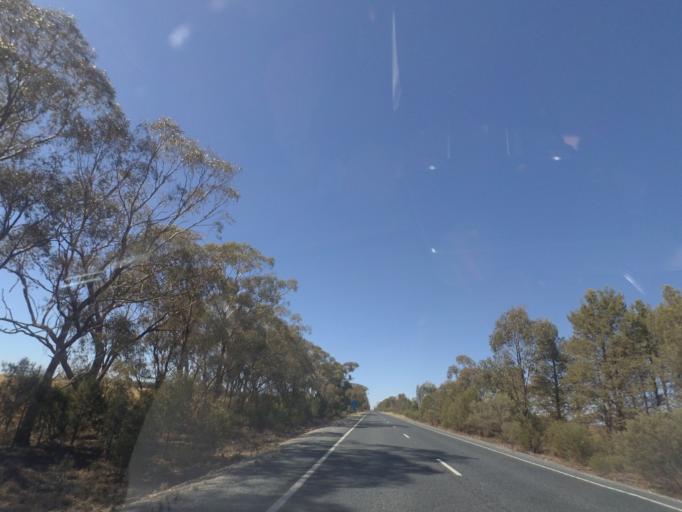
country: AU
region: New South Wales
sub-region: Bland
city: West Wyalong
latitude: -34.1557
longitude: 147.1176
